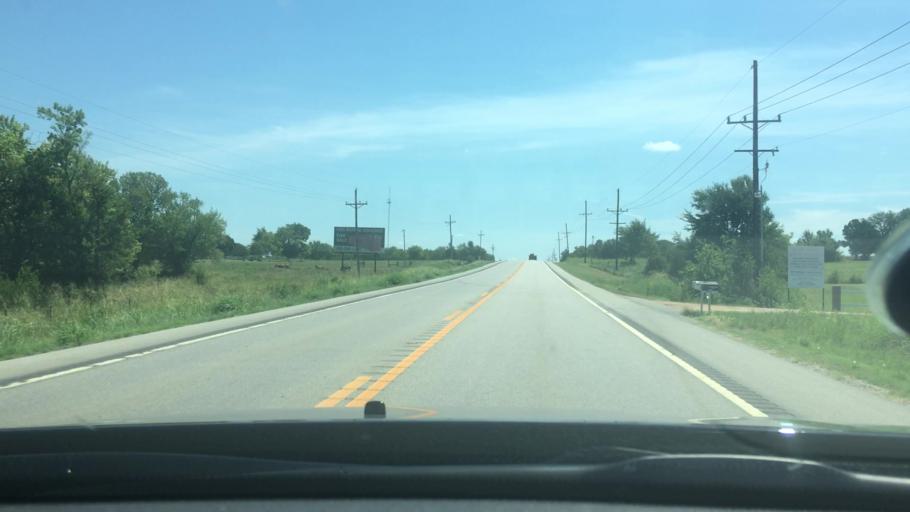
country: US
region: Oklahoma
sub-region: Bryan County
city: Durant
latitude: 33.9975
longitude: -96.2816
